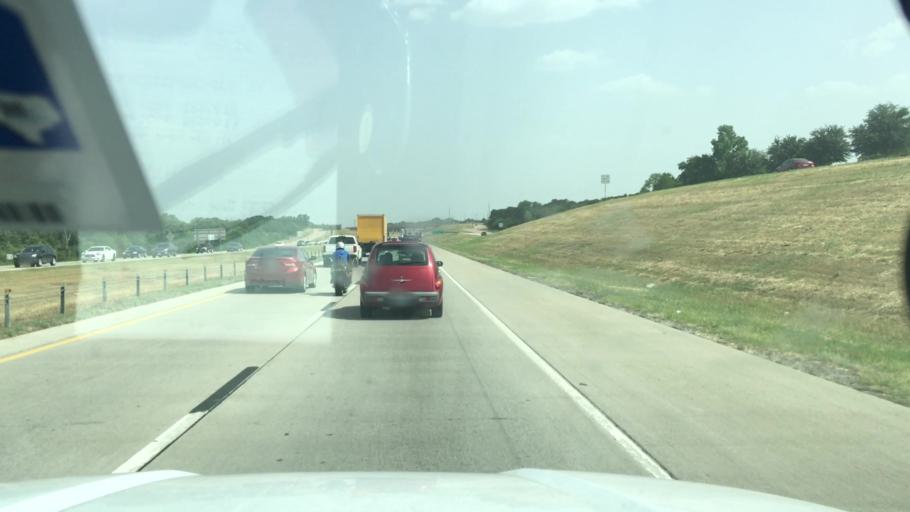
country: US
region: Texas
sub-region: Tarrant County
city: Grapevine
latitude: 32.8887
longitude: -97.0804
